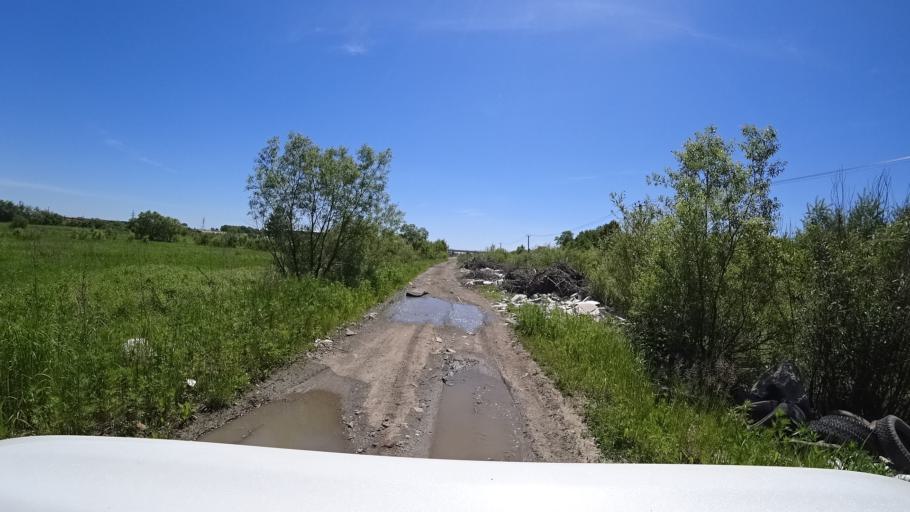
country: RU
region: Khabarovsk Krai
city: Topolevo
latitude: 48.4862
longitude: 135.1765
